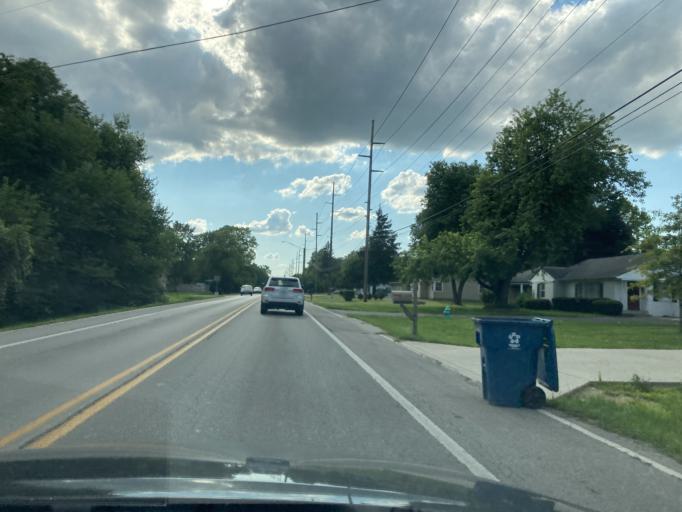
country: US
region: Indiana
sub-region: Marion County
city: Meridian Hills
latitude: 39.8536
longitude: -86.2147
